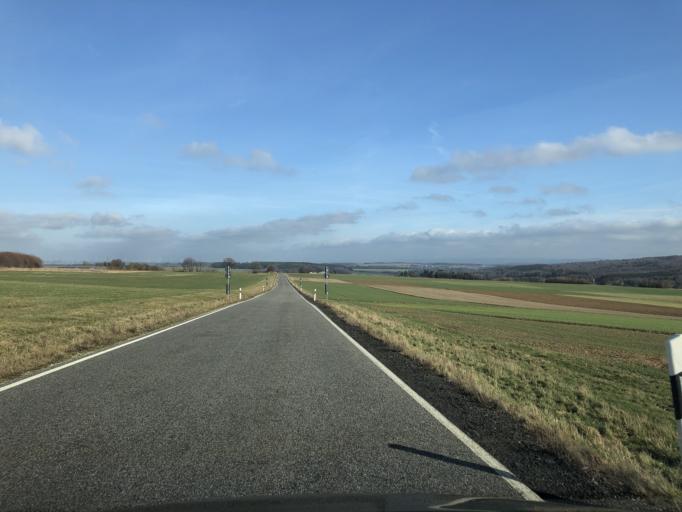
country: DE
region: Rheinland-Pfalz
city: Hochscheid
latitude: 49.8811
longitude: 7.2192
